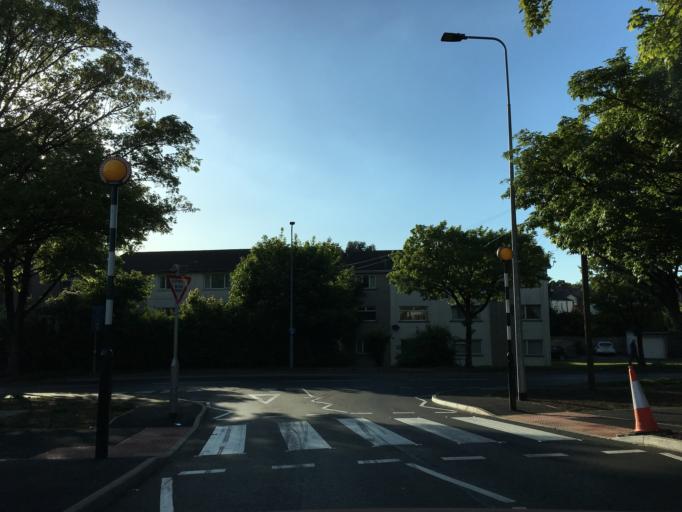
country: GB
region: Wales
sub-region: Newport
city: Marshfield
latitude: 51.5033
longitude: -3.1214
